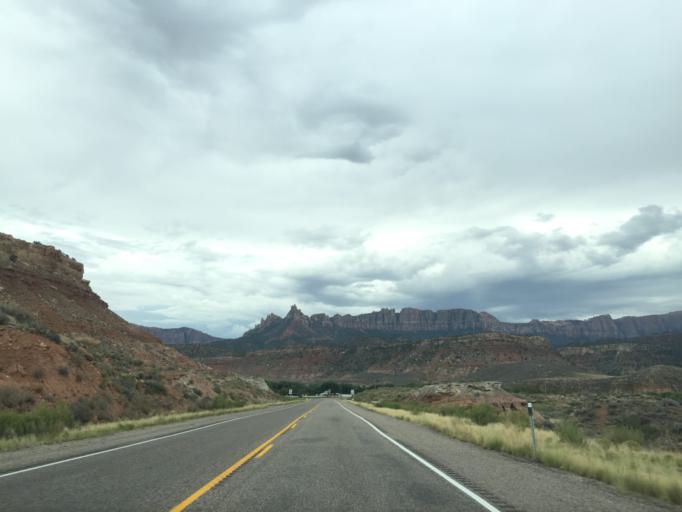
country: US
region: Utah
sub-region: Washington County
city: Hildale
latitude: 37.1667
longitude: -113.0633
